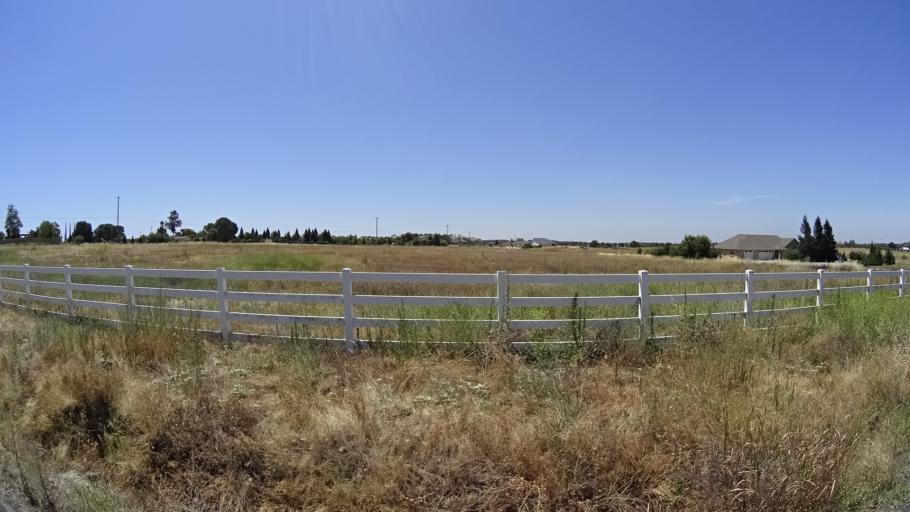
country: US
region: California
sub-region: Calaveras County
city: Rancho Calaveras
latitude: 38.1486
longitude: -120.9157
